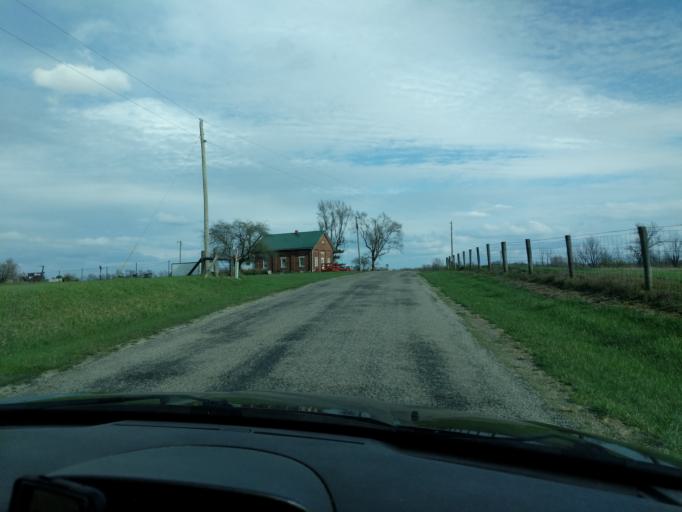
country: US
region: Ohio
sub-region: Champaign County
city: North Lewisburg
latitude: 40.1944
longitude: -83.6530
